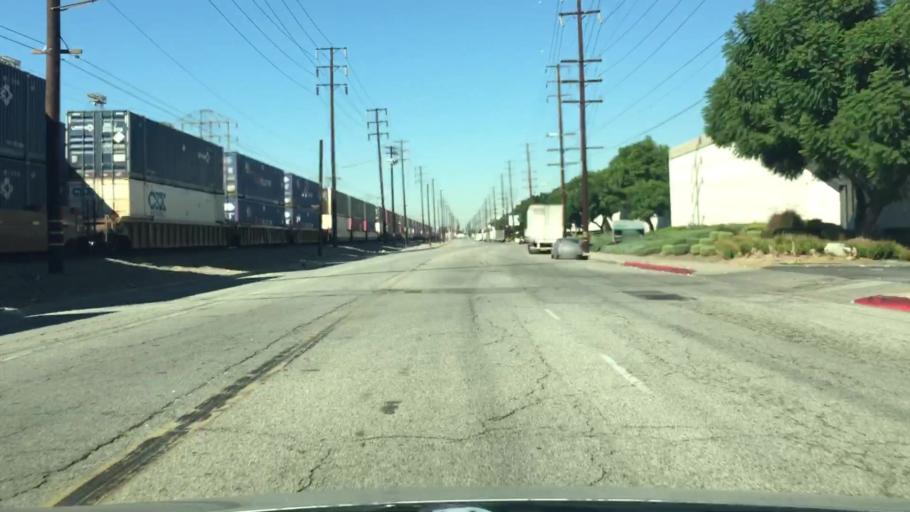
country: US
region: California
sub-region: Los Angeles County
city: Bell Gardens
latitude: 33.9782
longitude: -118.1520
